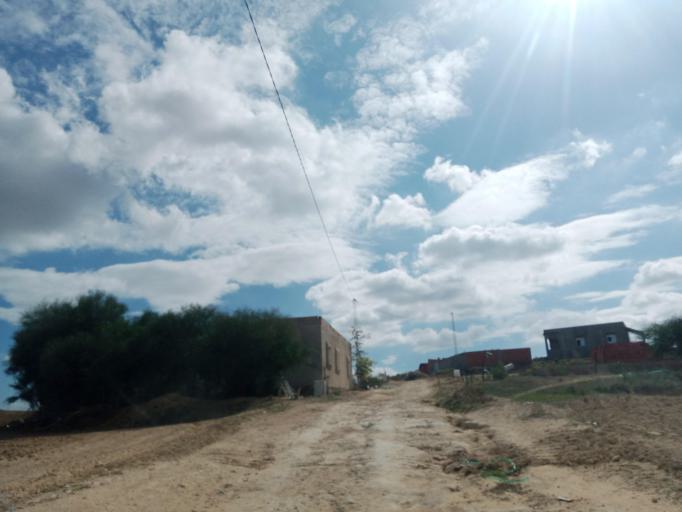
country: TN
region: Tunis
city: Oued Lill
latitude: 36.8100
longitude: 9.9824
